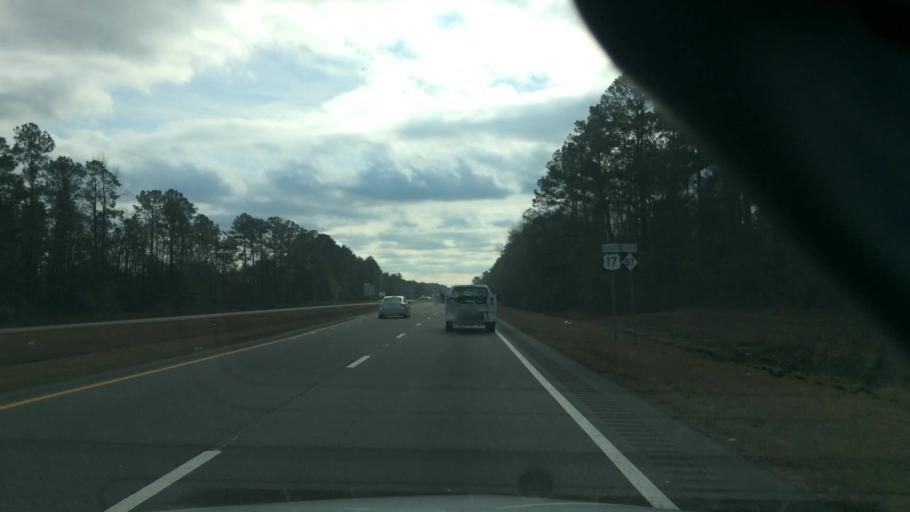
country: US
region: North Carolina
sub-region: Brunswick County
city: Leland
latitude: 34.1719
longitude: -78.0879
